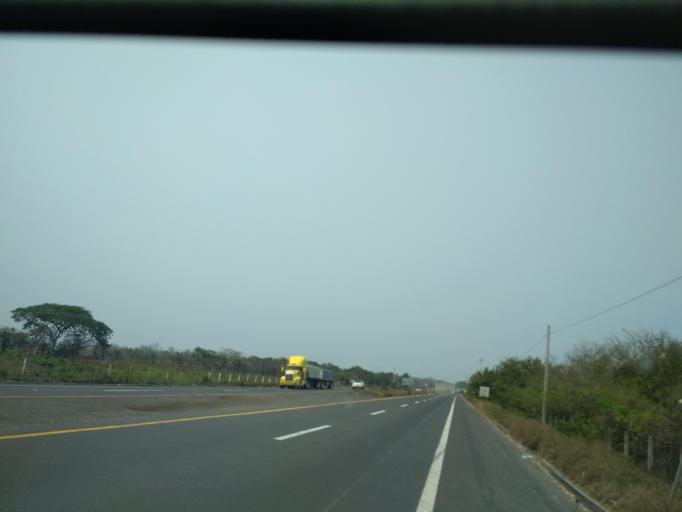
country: MX
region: Veracruz
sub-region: Veracruz
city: Delfino Victoria (Santa Fe)
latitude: 19.1980
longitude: -96.2727
